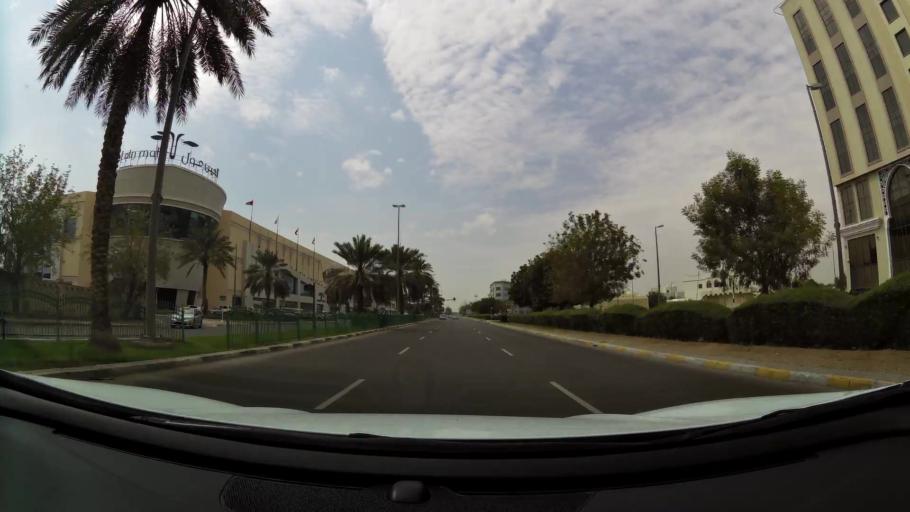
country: OM
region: Al Buraimi
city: Al Buraymi
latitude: 24.2240
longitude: 55.7830
